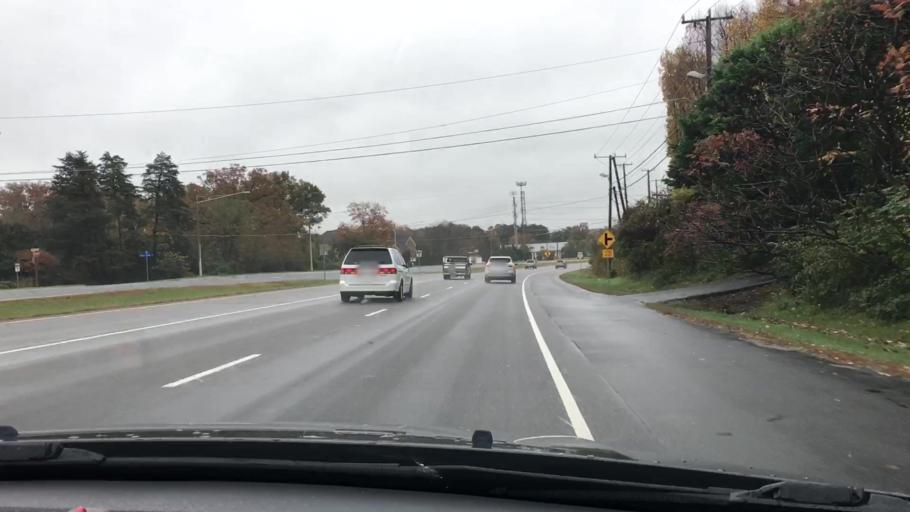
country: US
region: Virginia
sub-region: Prince William County
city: Lake Ridge
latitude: 38.7182
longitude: -77.2693
